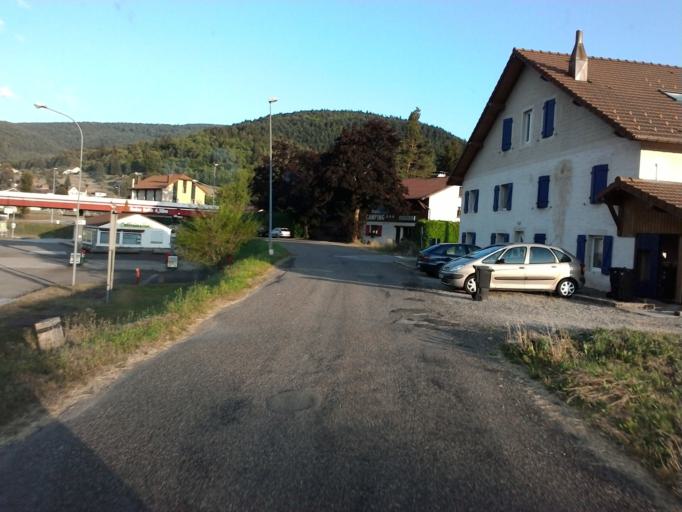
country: FR
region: Lorraine
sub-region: Departement des Vosges
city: Saint-Maurice-sur-Moselle
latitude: 47.8559
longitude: 6.8107
